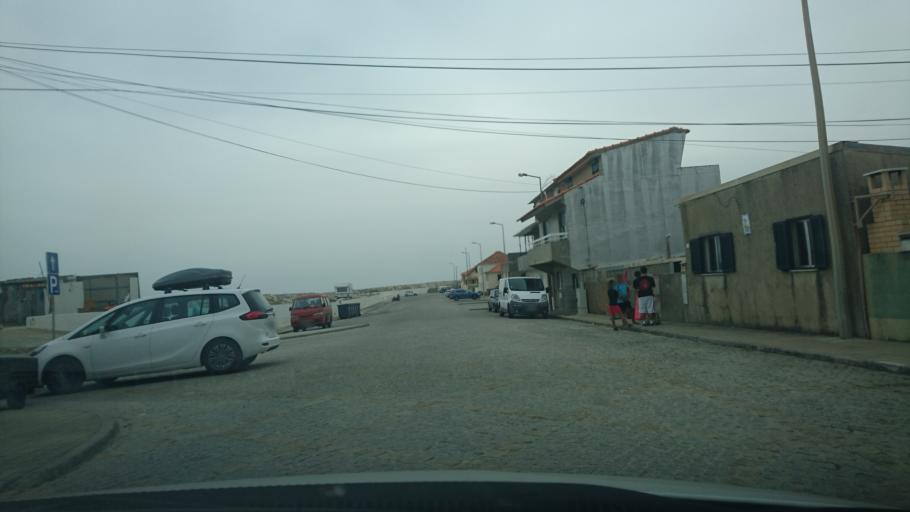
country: PT
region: Aveiro
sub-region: Ovar
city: Esmoriz
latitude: 40.9525
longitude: -8.6560
